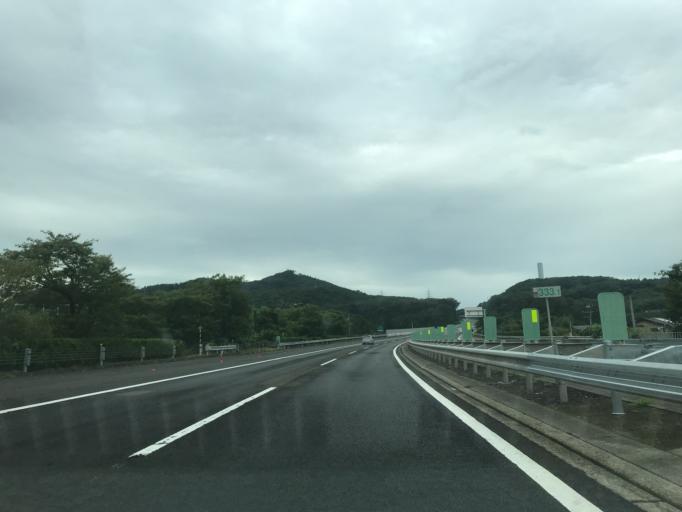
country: JP
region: Miyagi
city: Sendai
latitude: 38.2644
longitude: 140.8094
